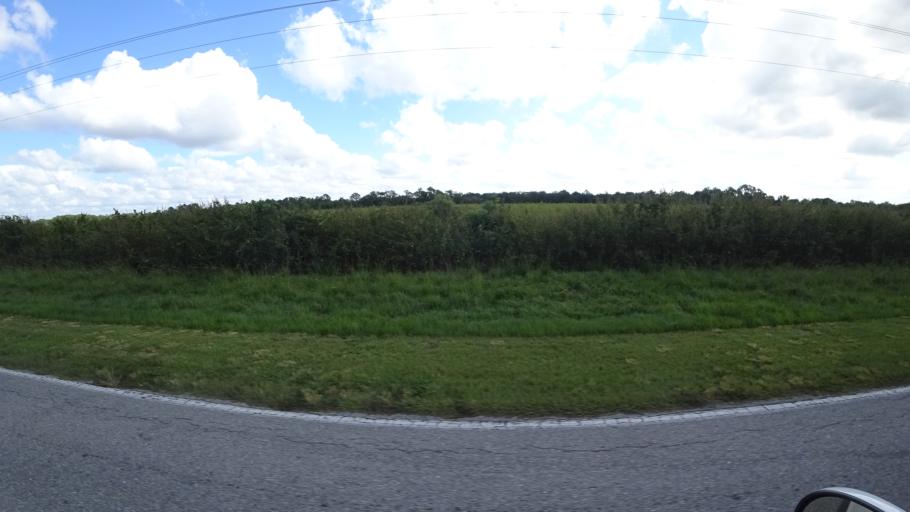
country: US
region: Florida
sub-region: Sarasota County
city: Lake Sarasota
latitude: 27.3703
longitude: -82.1413
